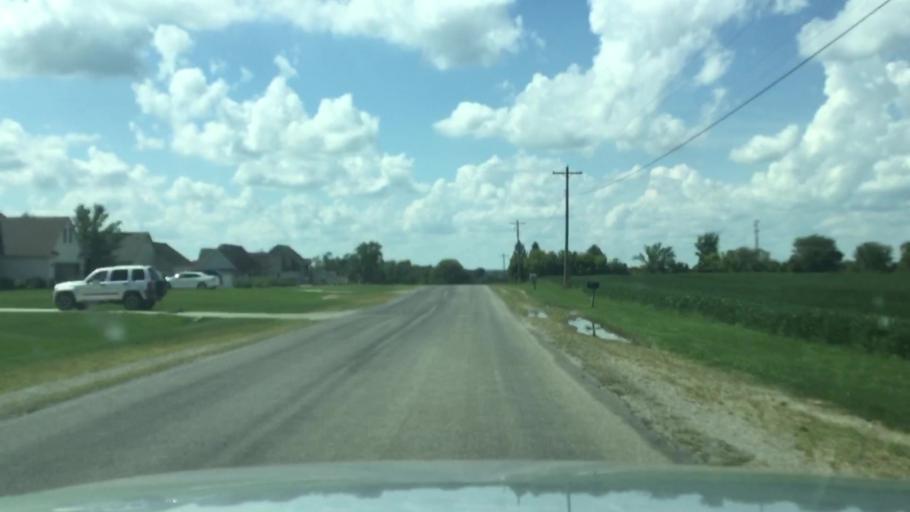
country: US
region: Michigan
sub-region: Lenawee County
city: Clinton
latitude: 42.0725
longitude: -83.9513
